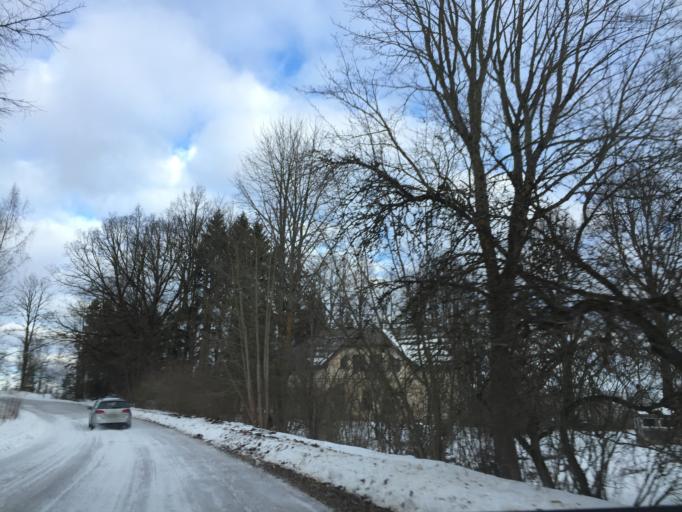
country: LV
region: Lielvarde
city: Lielvarde
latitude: 56.5761
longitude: 24.7371
